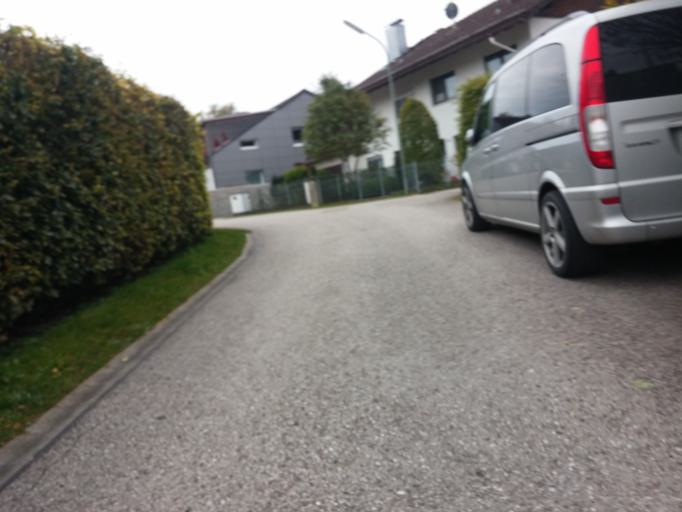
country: DE
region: Bavaria
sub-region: Upper Bavaria
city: Kirchseeon
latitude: 48.0746
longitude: 11.8824
